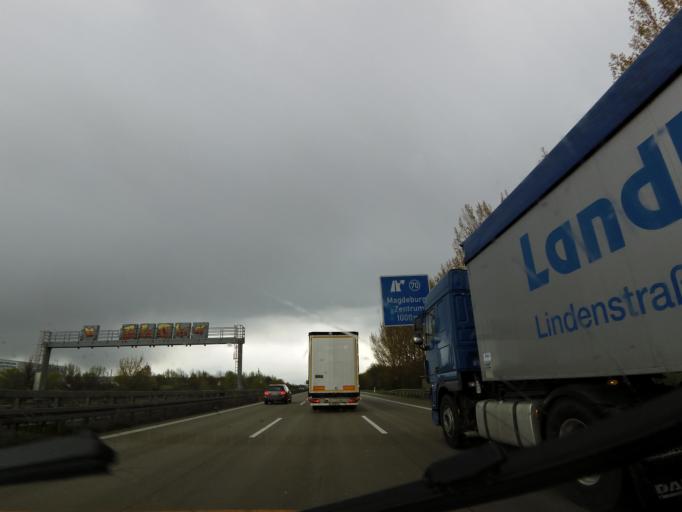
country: DE
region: Saxony-Anhalt
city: Ebendorf
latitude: 52.1797
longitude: 11.5930
